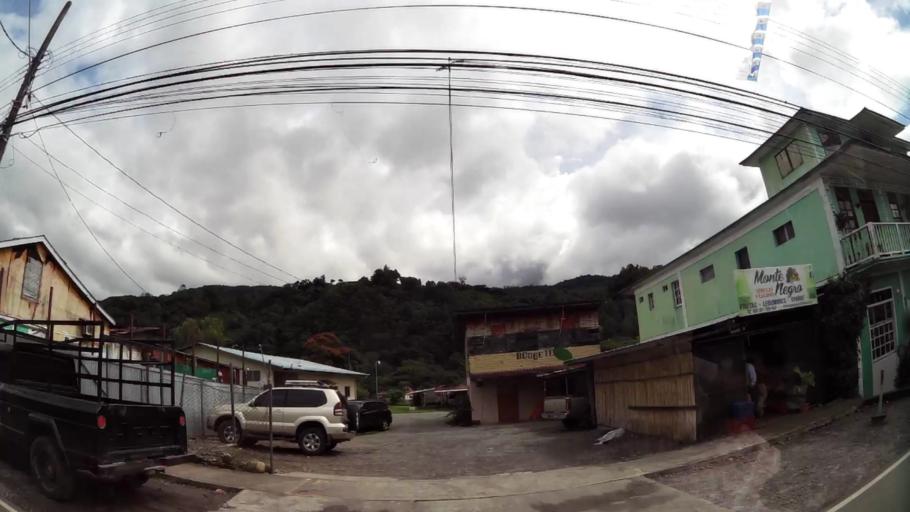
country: PA
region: Chiriqui
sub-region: Distrito Boquete
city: Boquete
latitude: 8.7778
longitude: -82.4318
